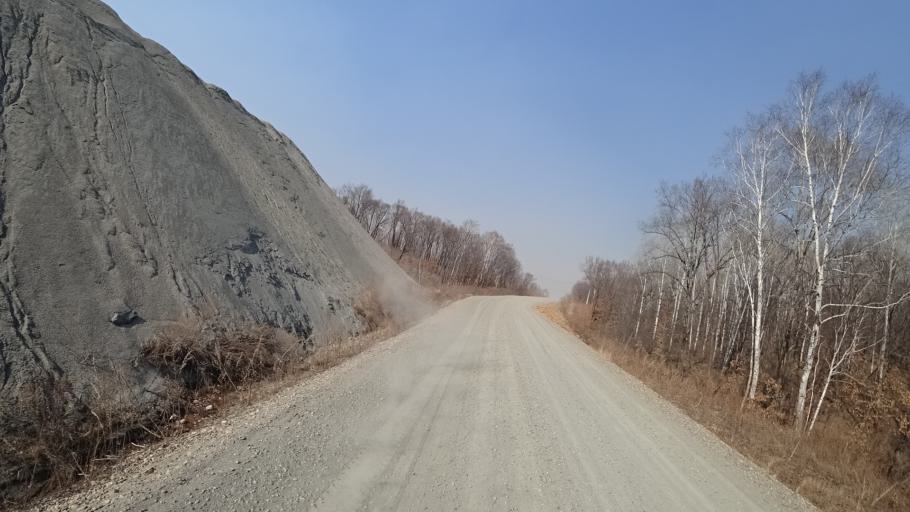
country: RU
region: Amur
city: Novobureyskiy
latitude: 49.7990
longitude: 129.9584
